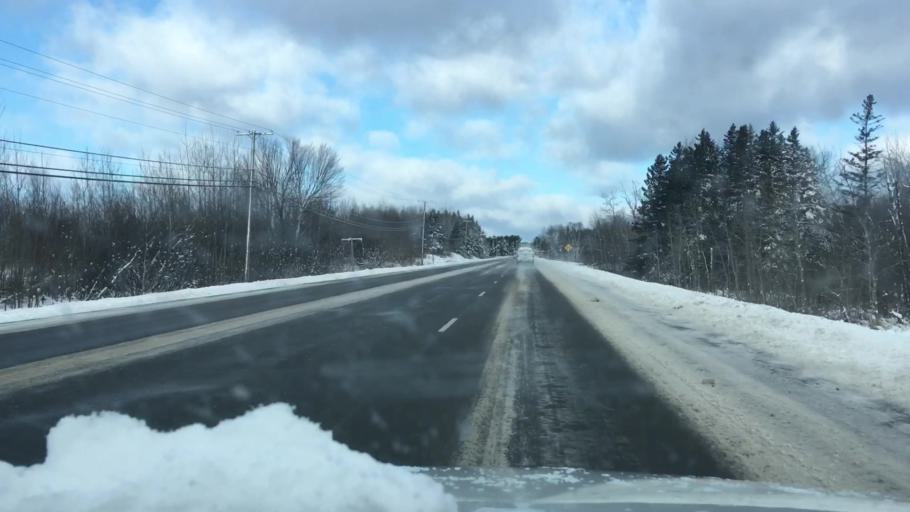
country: US
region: Maine
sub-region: Aroostook County
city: Caribou
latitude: 46.8746
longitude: -68.0046
